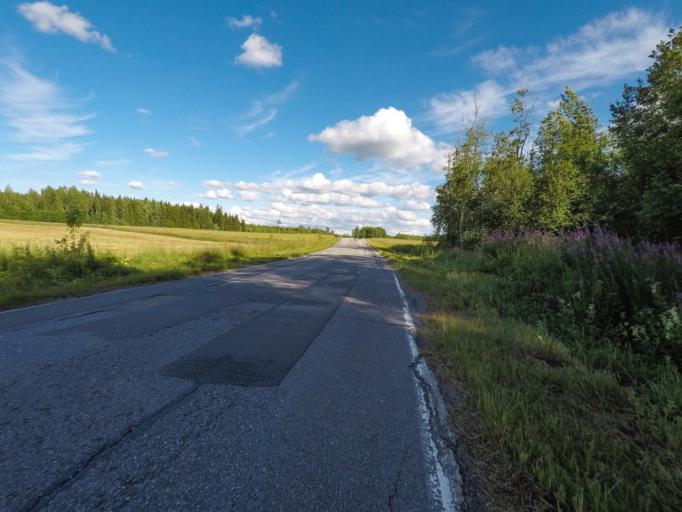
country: FI
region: South Karelia
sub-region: Imatra
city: Imatra
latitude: 61.1373
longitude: 28.6509
